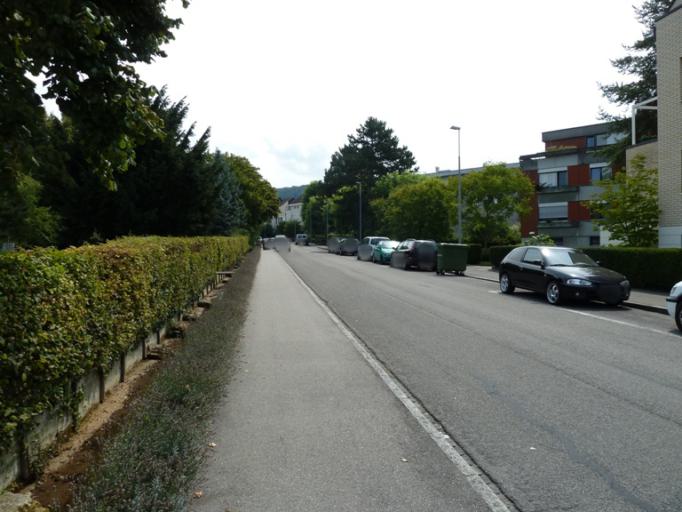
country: CH
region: Basel-City
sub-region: Basel-Stadt
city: Riehen
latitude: 47.5826
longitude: 7.6521
